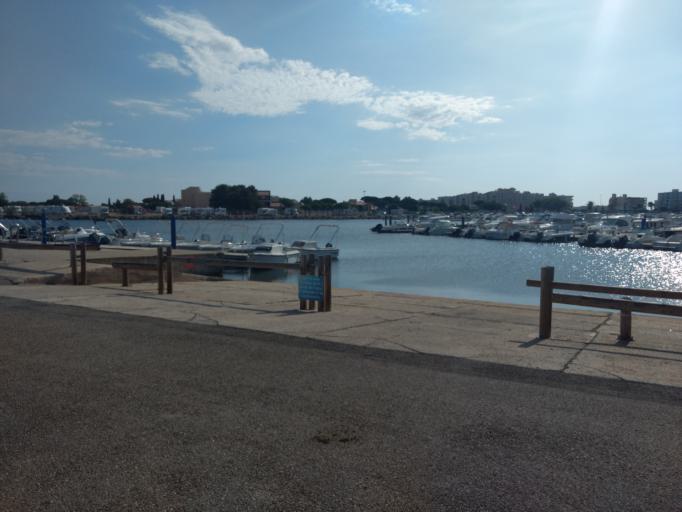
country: FR
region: Languedoc-Roussillon
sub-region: Departement des Pyrenees-Orientales
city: Le Barcares
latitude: 42.7998
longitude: 3.0310
